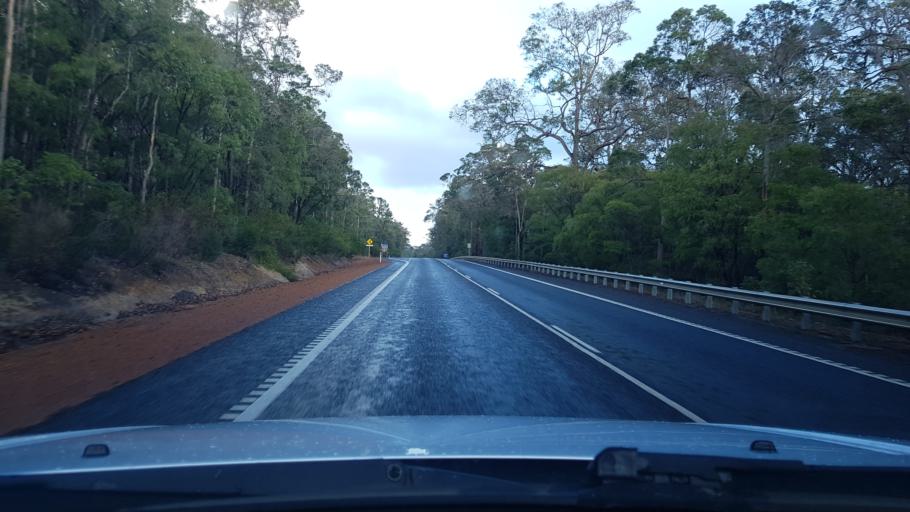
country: AU
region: Western Australia
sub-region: Augusta-Margaret River Shire
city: Margaret River
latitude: -33.9132
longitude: 115.0837
